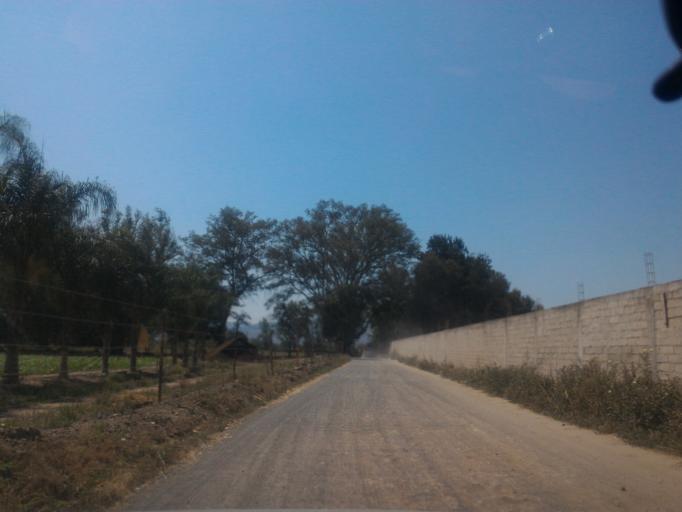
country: MX
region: Jalisco
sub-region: San Pedro Tlaquepaque
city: Paseo del Prado
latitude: 20.5631
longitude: -103.3988
